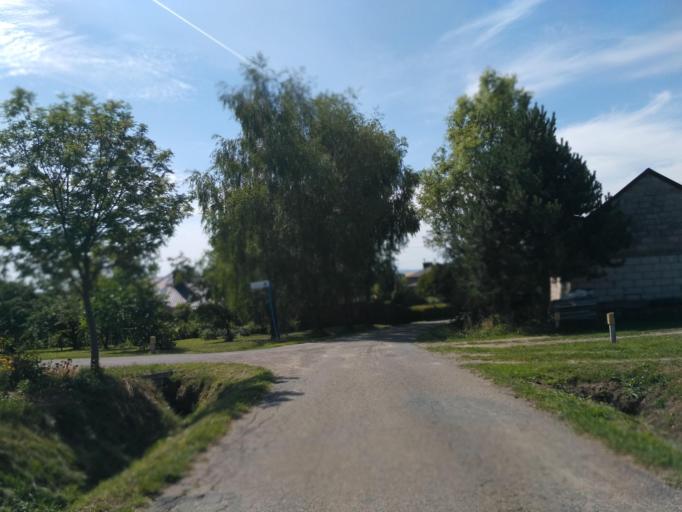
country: PL
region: Subcarpathian Voivodeship
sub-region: Powiat krosnienski
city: Korczyna
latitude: 49.7129
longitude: 21.8287
